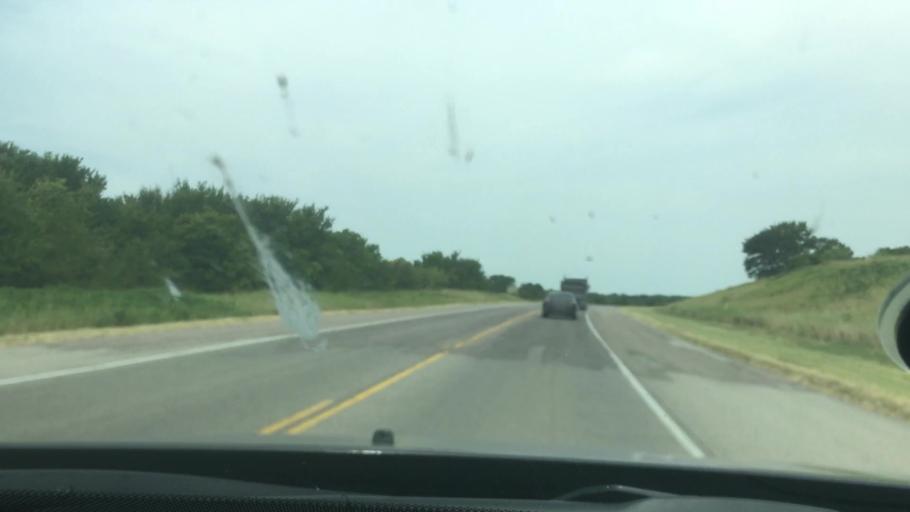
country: US
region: Oklahoma
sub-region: Pontotoc County
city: Ada
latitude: 34.6438
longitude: -96.5448
